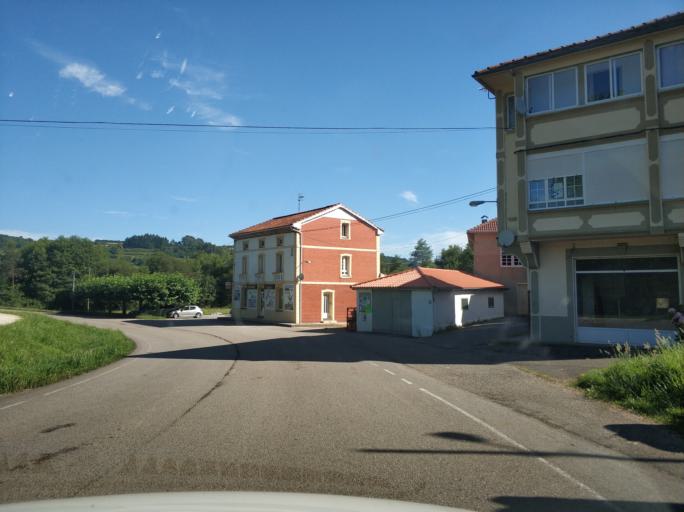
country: ES
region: Asturias
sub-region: Province of Asturias
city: Cudillero
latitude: 43.5579
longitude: -6.2281
